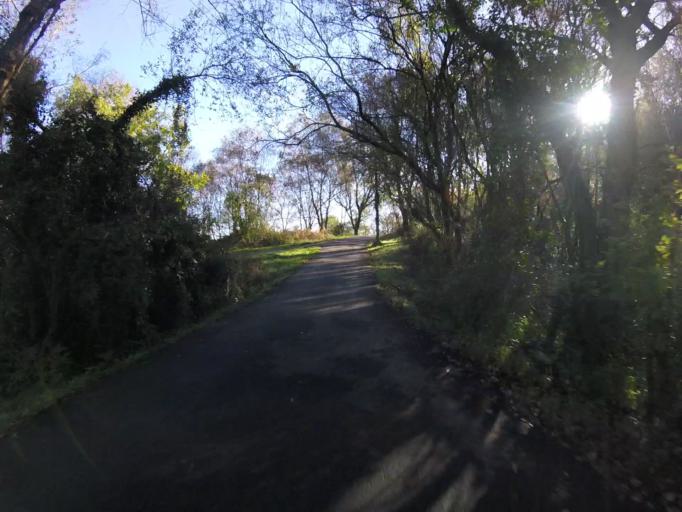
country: ES
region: Basque Country
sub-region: Provincia de Guipuzcoa
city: Usurbil
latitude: 43.2964
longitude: -2.0535
